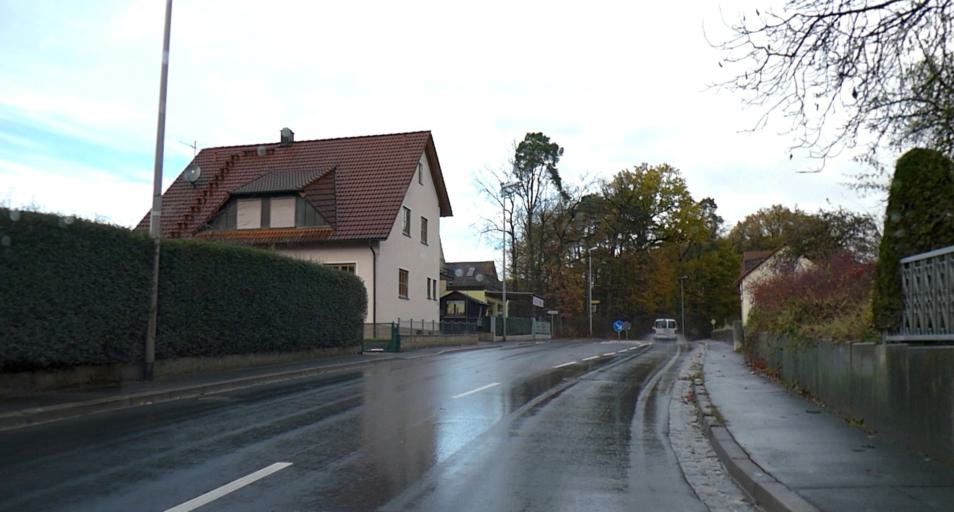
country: DE
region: Bavaria
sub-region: Upper Franconia
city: Effeltrich
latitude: 49.6603
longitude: 11.0985
